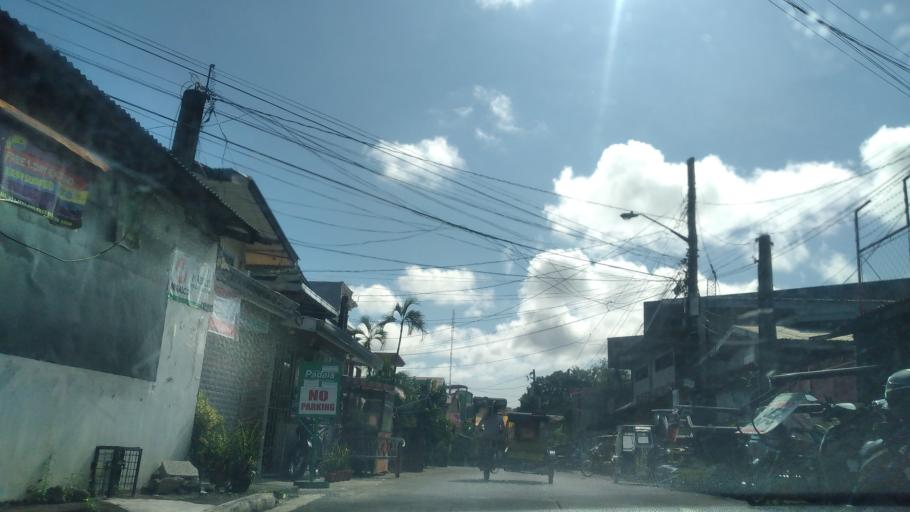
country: PH
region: Calabarzon
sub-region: Province of Quezon
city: Lucena
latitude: 13.9384
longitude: 121.6100
